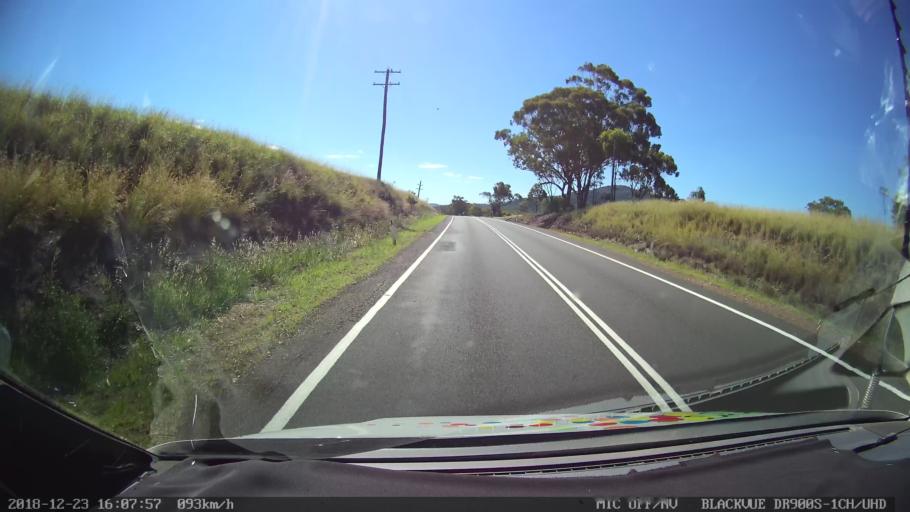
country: AU
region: New South Wales
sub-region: Tamworth Municipality
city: Phillip
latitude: -31.2675
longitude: 150.7544
